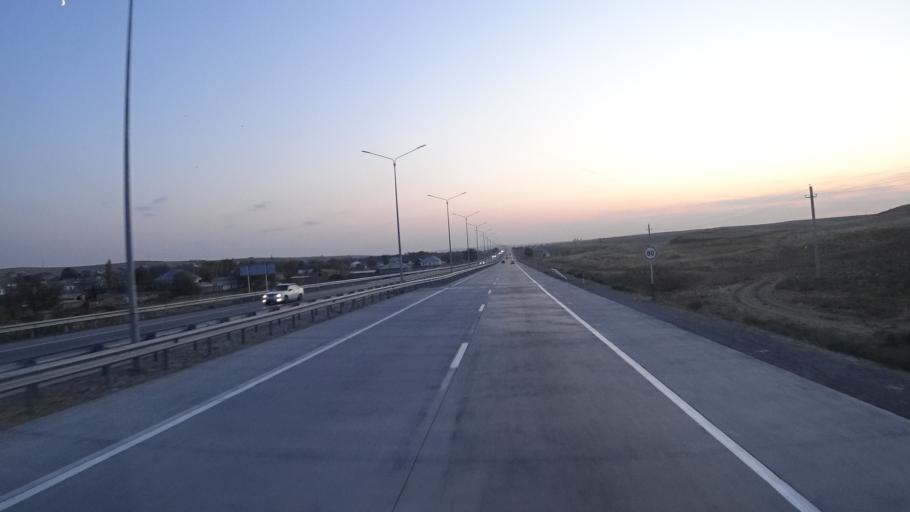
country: KZ
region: Ongtustik Qazaqstan
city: Qazyqurt
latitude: 41.8945
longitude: 69.4514
